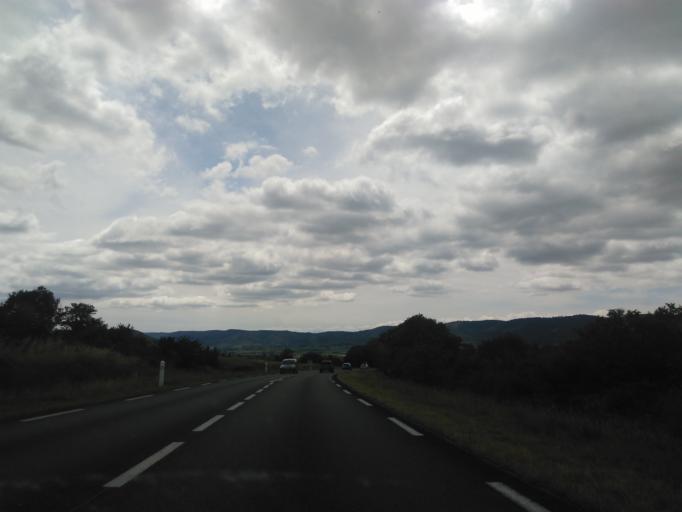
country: FR
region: Rhone-Alpes
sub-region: Departement de l'Ardeche
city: Alba-la-Romaine
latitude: 44.5717
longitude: 4.6225
